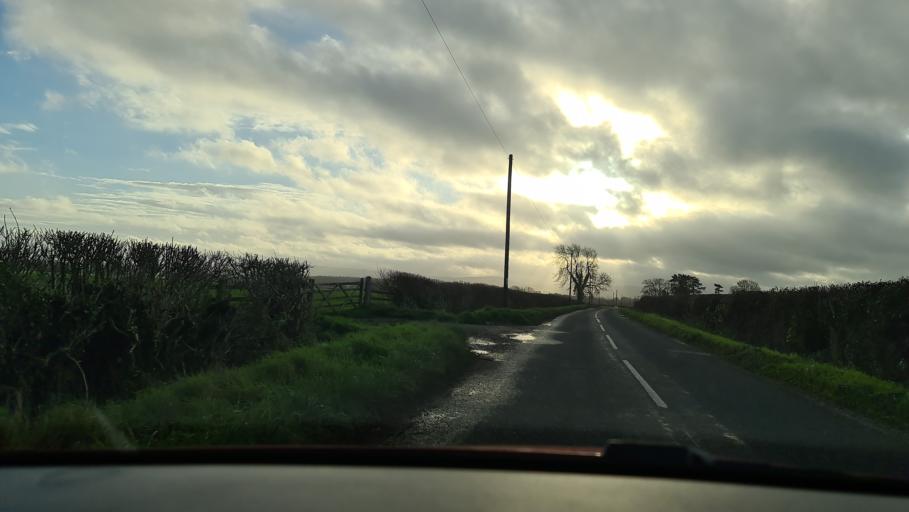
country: GB
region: England
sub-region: Buckinghamshire
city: Stone
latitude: 51.7859
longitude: -0.8847
